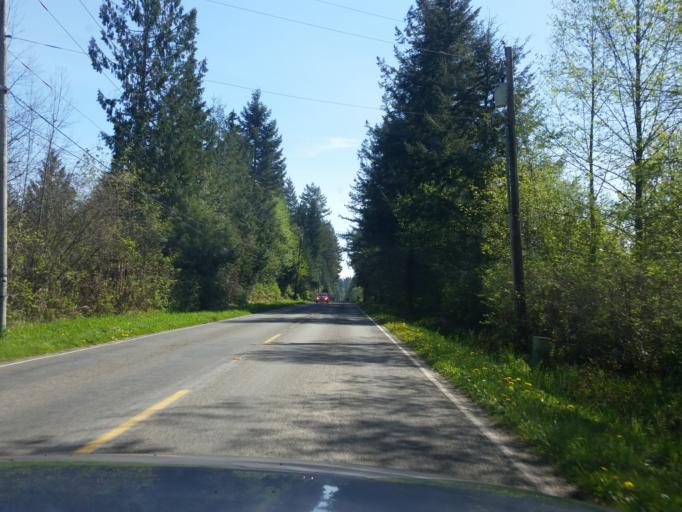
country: US
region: Washington
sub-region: Snohomish County
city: Machias
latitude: 47.9634
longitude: -122.0375
